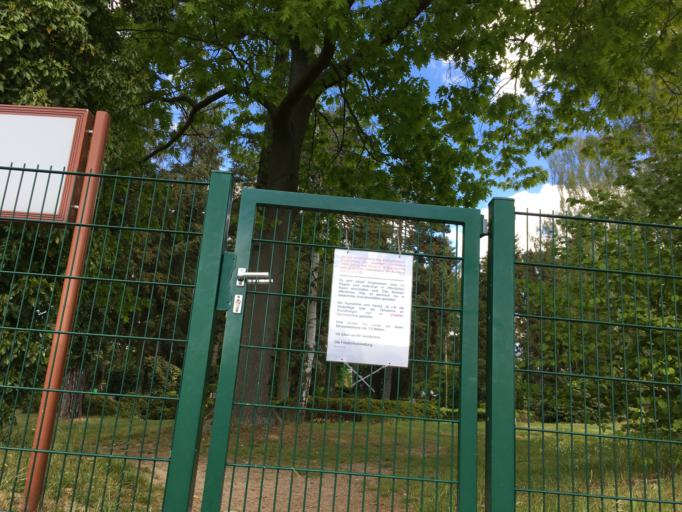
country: DE
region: Brandenburg
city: Biesenthal
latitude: 52.7617
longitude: 13.6351
